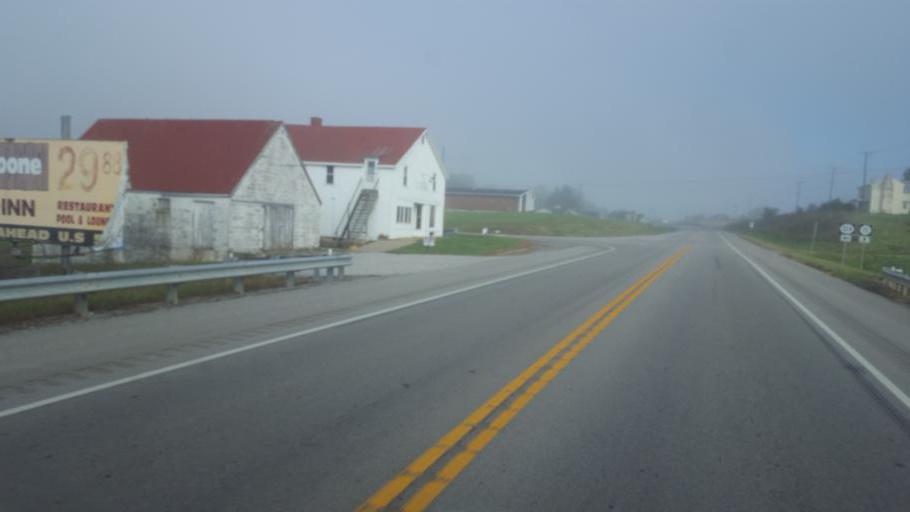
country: US
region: Kentucky
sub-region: Fleming County
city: Flemingsburg
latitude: 38.4981
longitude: -83.7563
